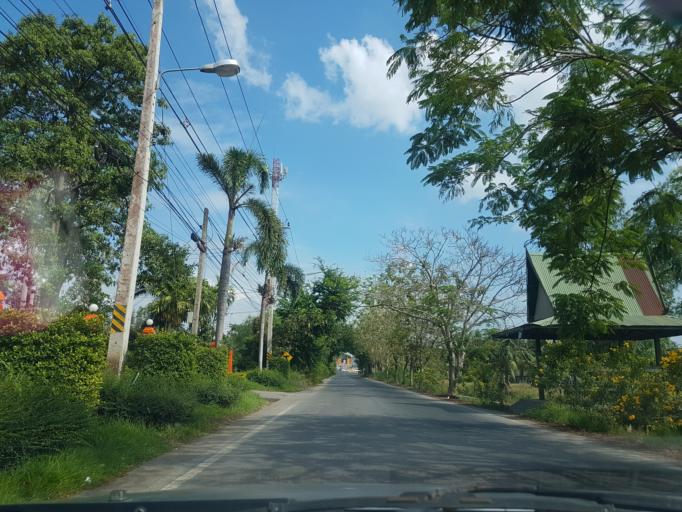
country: TH
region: Pathum Thani
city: Nong Suea
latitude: 14.1354
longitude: 100.8899
